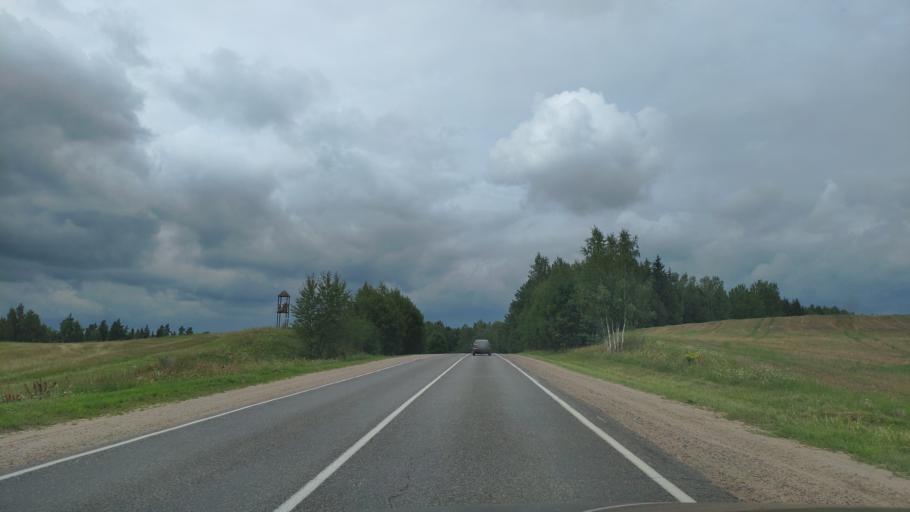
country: BY
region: Minsk
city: Zaslawye
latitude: 53.9623
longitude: 27.2448
